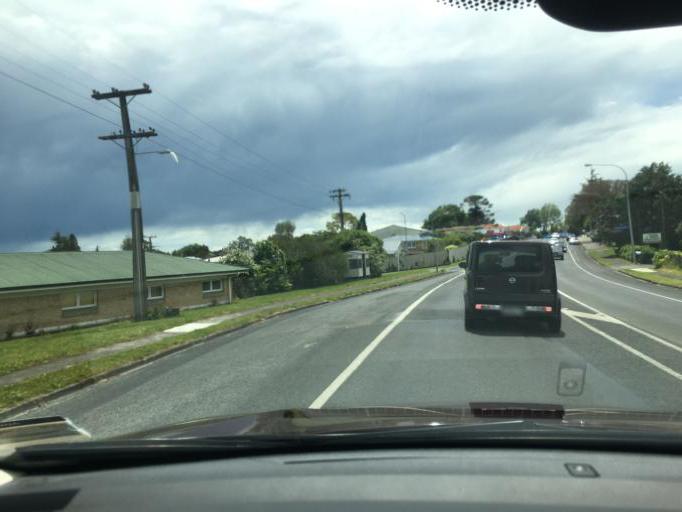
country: NZ
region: Waikato
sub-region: Waipa District
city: Cambridge
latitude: -37.9205
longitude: 175.3078
